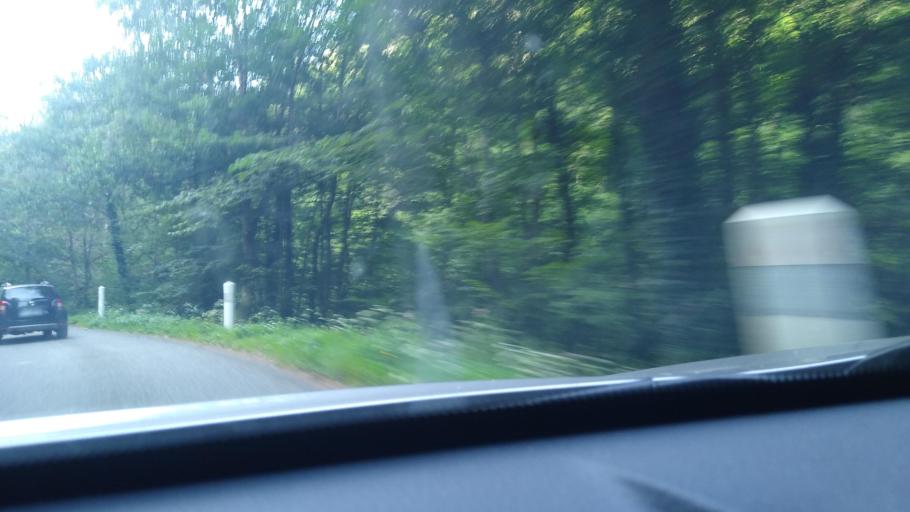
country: FR
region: Midi-Pyrenees
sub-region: Departement de l'Ariege
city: Saint-Girons
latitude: 42.8058
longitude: 1.1949
